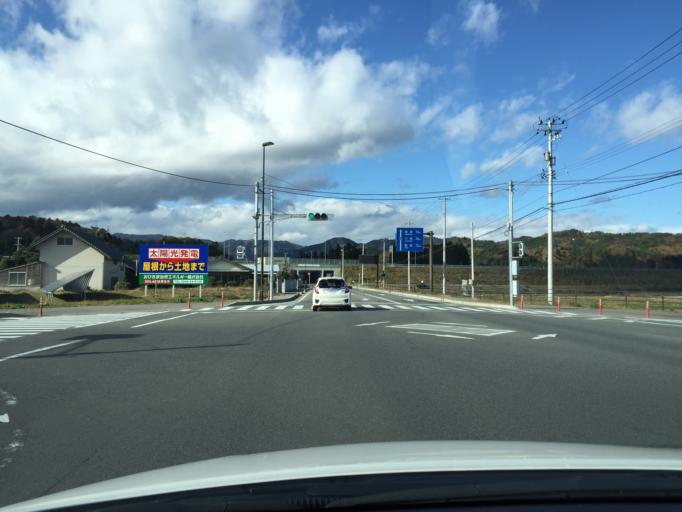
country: JP
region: Fukushima
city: Namie
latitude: 37.6606
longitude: 140.9231
